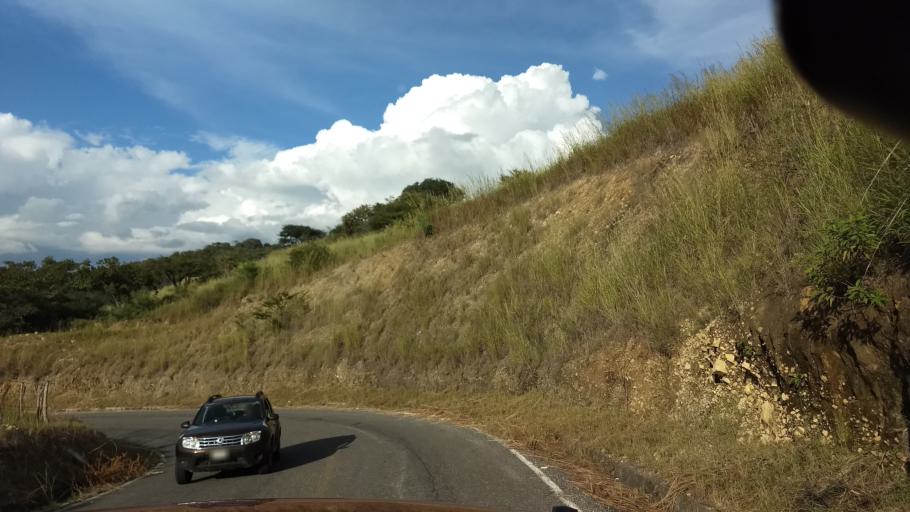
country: MX
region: Colima
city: Suchitlan
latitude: 19.4593
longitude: -103.7935
